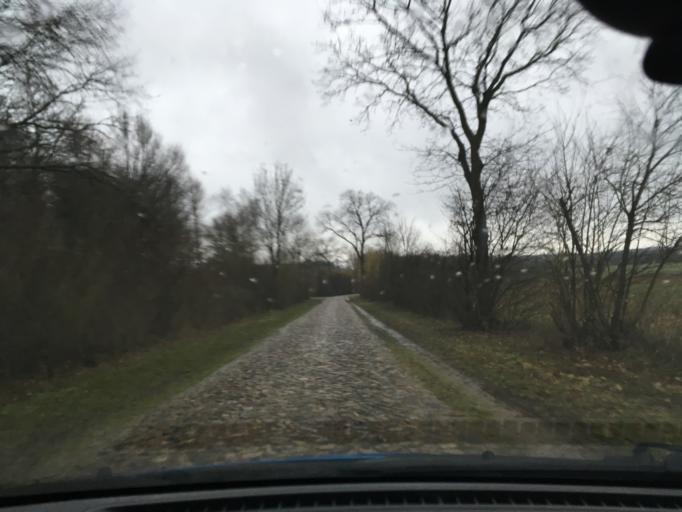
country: DE
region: Schleswig-Holstein
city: Kruzen
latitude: 53.4085
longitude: 10.5221
